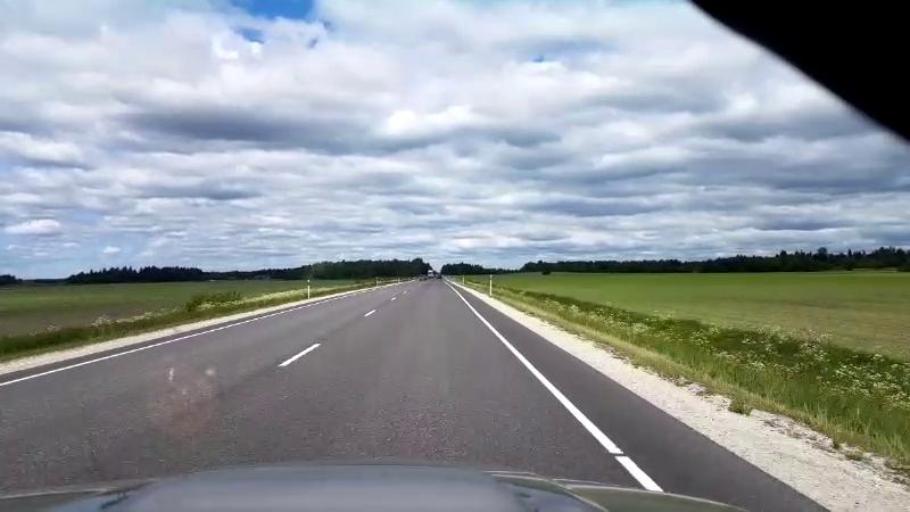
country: EE
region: Raplamaa
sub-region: Maerjamaa vald
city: Marjamaa
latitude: 58.8460
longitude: 24.4274
